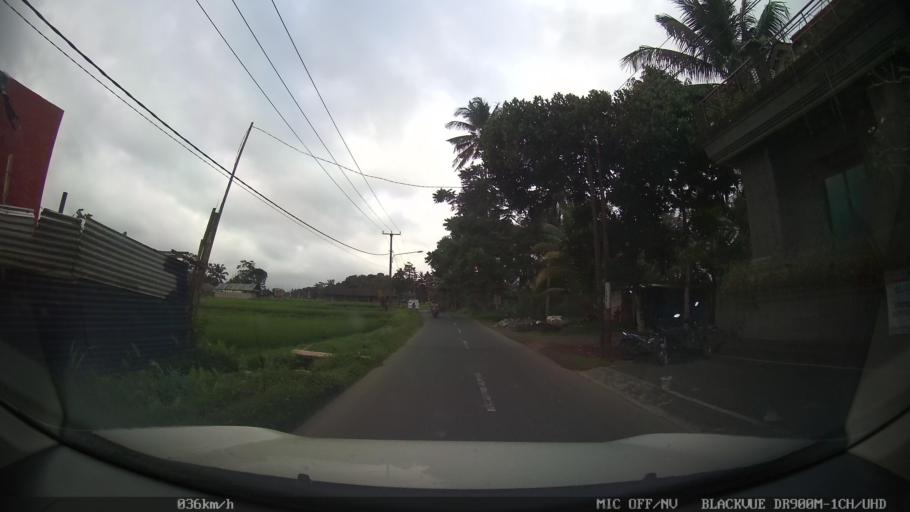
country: ID
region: Bali
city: Bunutan
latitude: -8.4810
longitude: 115.2582
